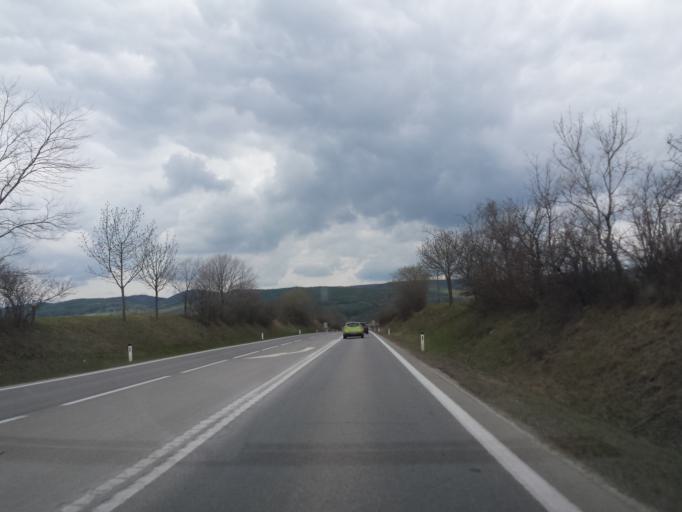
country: AT
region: Lower Austria
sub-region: Politischer Bezirk Krems
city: Lengenfeld
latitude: 48.4603
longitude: 15.5936
